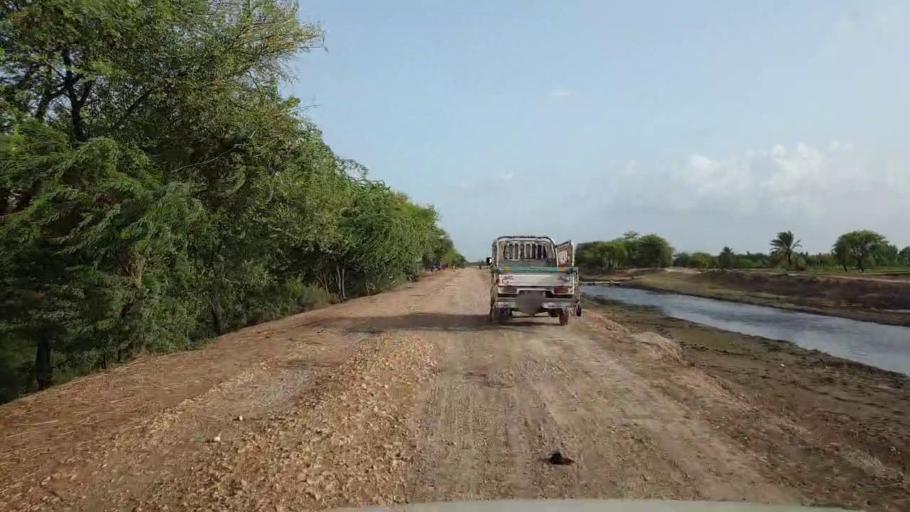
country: PK
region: Sindh
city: Kario
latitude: 24.8499
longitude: 68.6522
